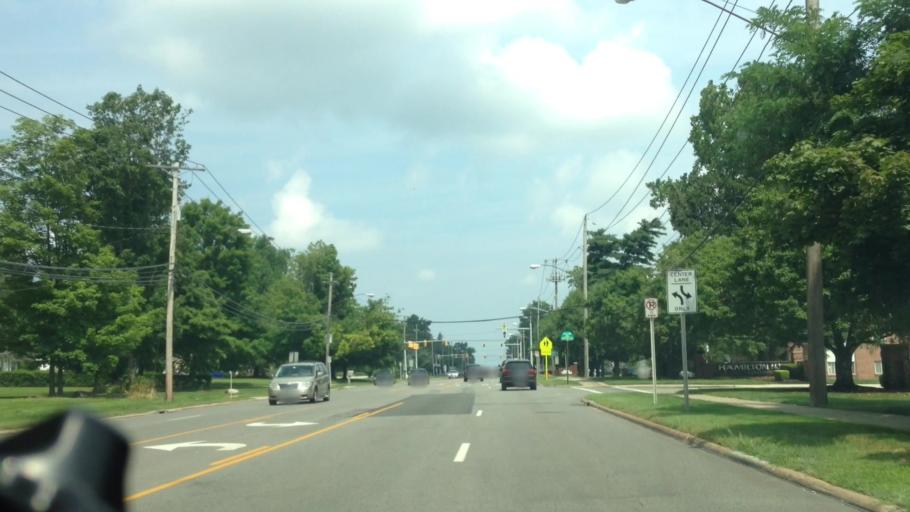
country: US
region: Ohio
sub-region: Cuyahoga County
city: Mayfield Heights
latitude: 41.5278
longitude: -81.4388
